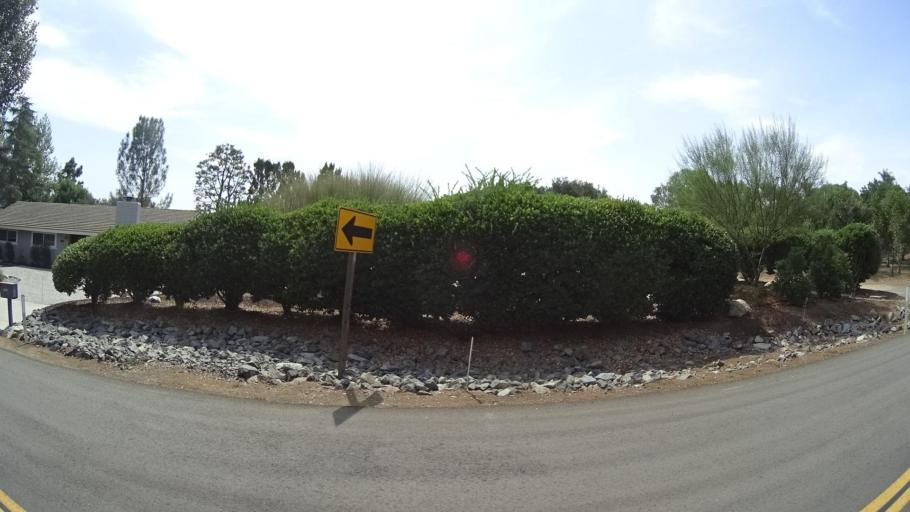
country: US
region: California
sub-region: San Diego County
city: Escondido
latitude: 33.0930
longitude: -117.0324
